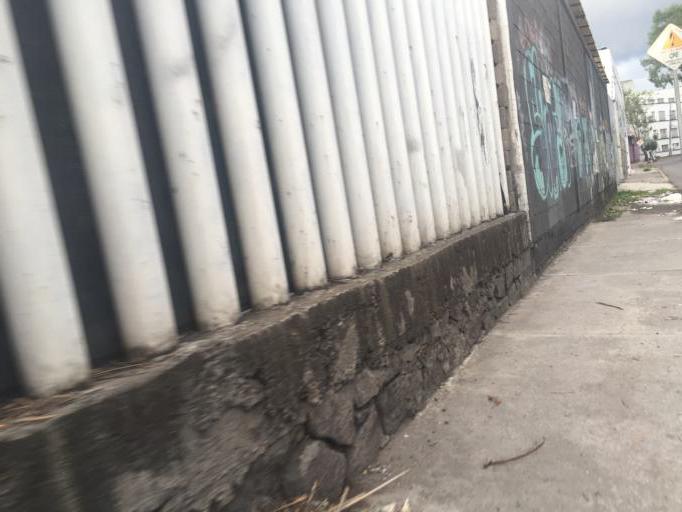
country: MX
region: Mexico City
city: Iztapalapa
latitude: 19.3534
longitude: -99.0818
